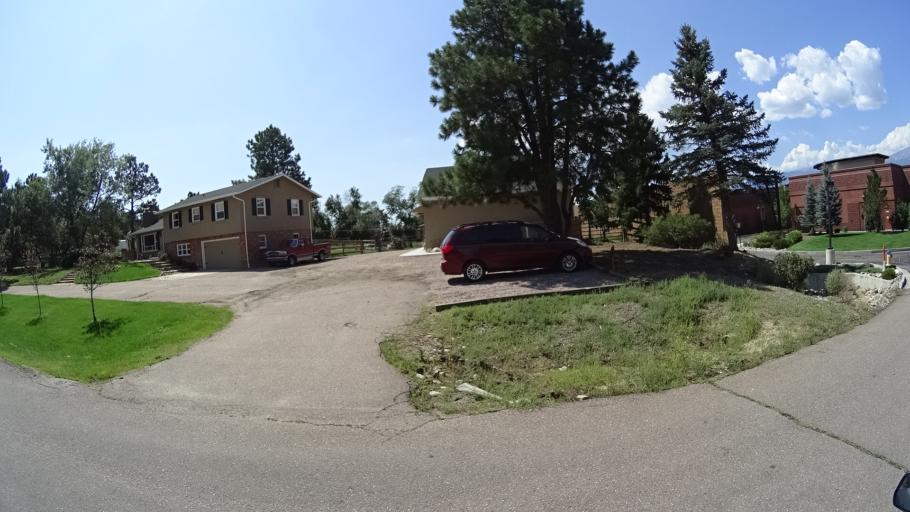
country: US
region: Colorado
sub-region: El Paso County
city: Air Force Academy
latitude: 38.9384
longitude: -104.7964
